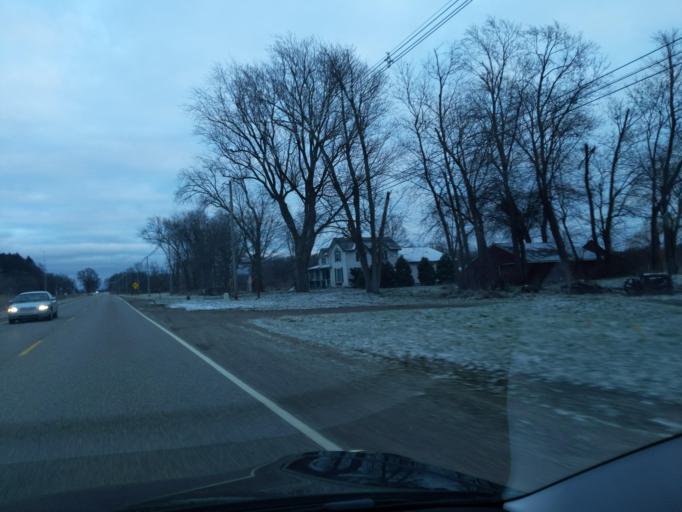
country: US
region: Michigan
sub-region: Jackson County
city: Spring Arbor
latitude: 42.2536
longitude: -84.5024
